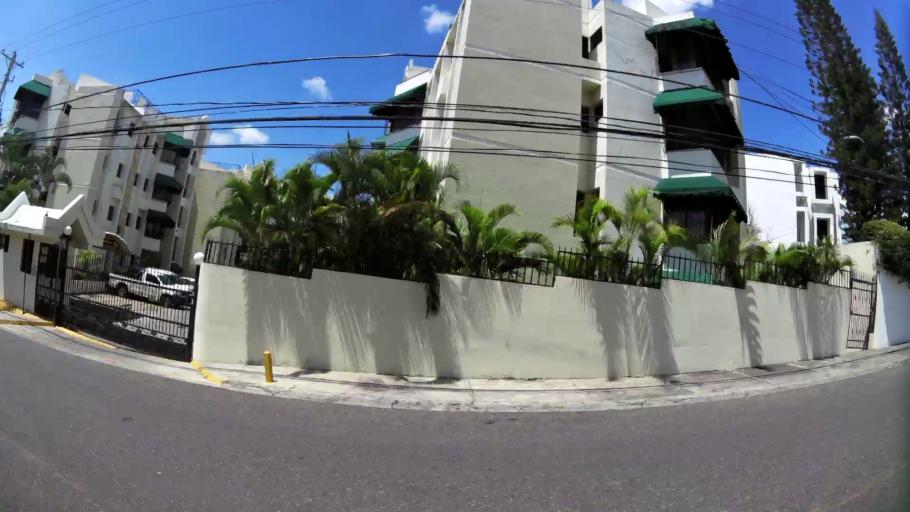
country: DO
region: Santiago
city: Santiago de los Caballeros
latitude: 19.4708
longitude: -70.6792
